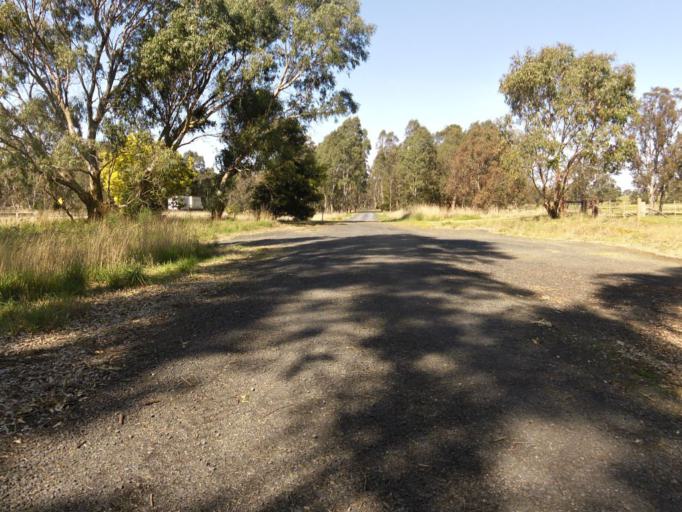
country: AU
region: Victoria
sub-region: Murrindindi
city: Alexandra
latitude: -36.9855
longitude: 145.7300
